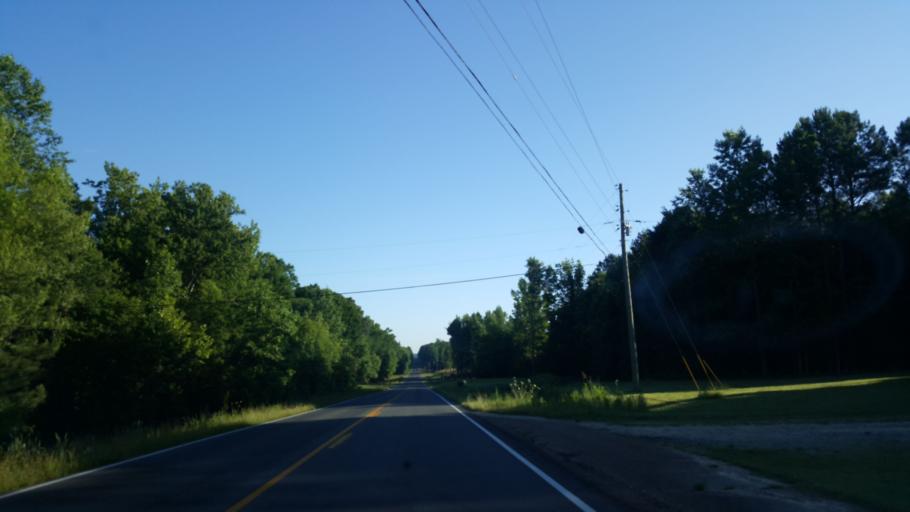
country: US
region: Tennessee
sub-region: Henderson County
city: Lexington
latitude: 35.5402
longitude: -88.3833
